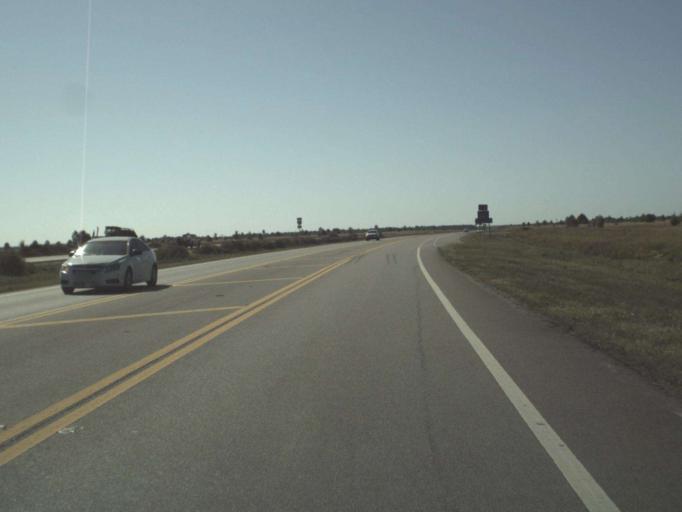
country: US
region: Florida
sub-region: Walton County
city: Freeport
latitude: 30.5545
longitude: -86.1065
